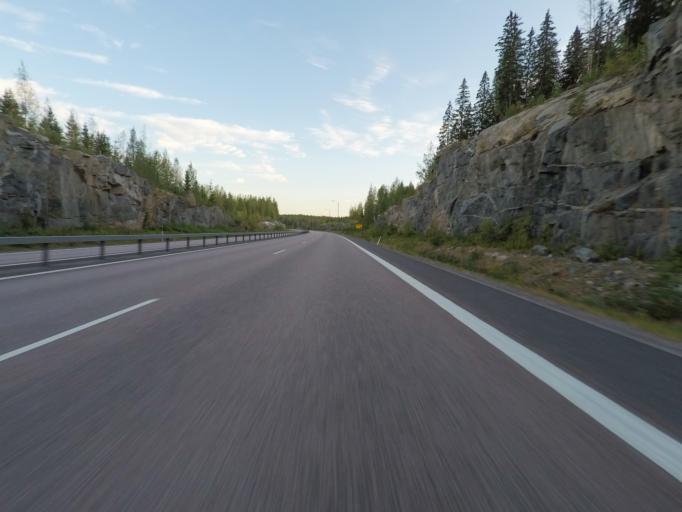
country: FI
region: Central Finland
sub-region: Jyvaeskylae
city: Saeynaetsalo
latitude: 62.2160
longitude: 25.8915
